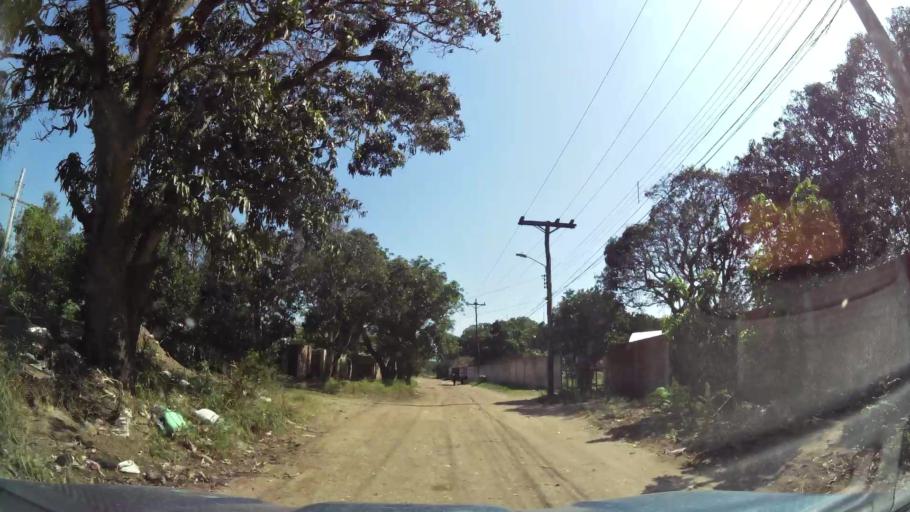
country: BO
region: Santa Cruz
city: Santa Cruz de la Sierra
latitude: -17.7323
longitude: -63.1592
